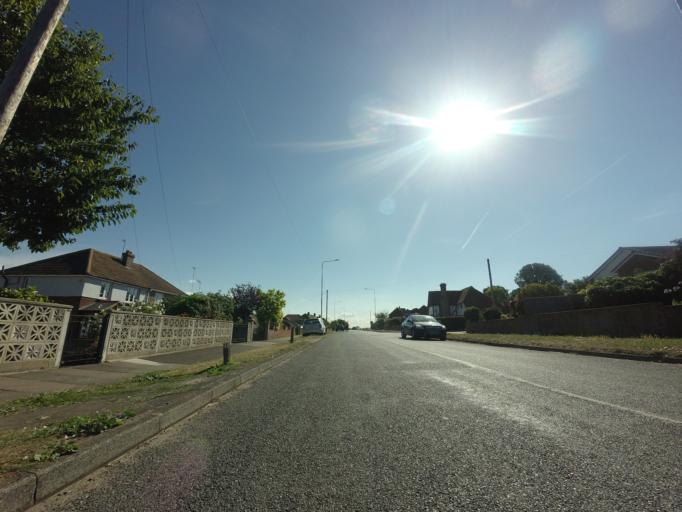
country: GB
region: England
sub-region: Kent
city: Gravesend
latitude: 51.4330
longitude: 0.4090
